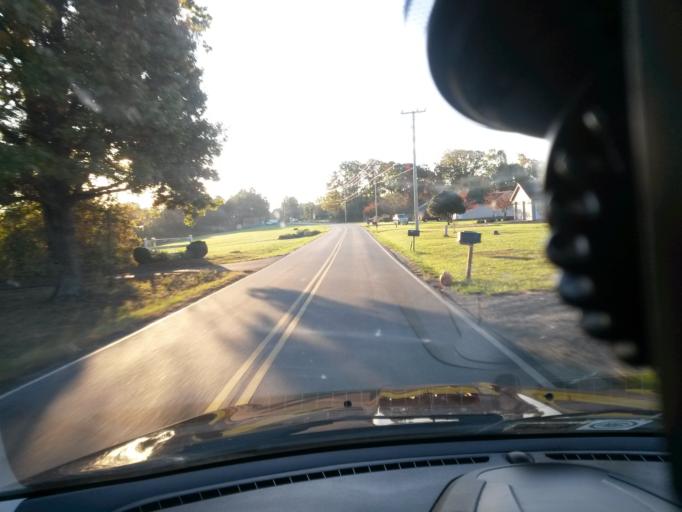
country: US
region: Virginia
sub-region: Franklin County
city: North Shore
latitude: 37.1292
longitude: -79.7669
